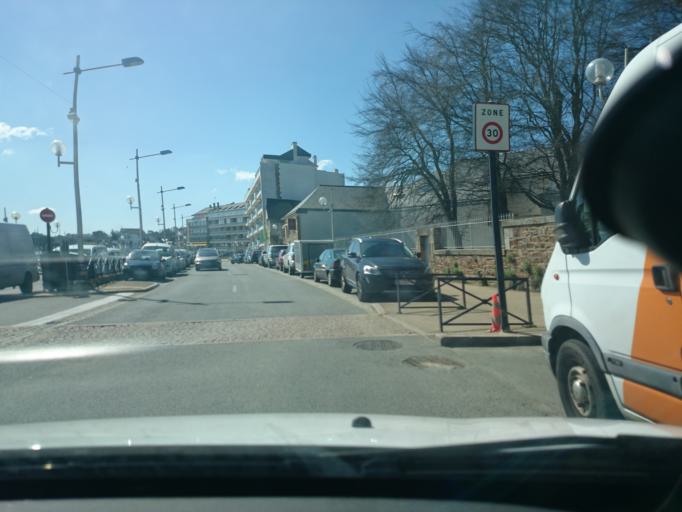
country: FR
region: Brittany
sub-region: Departement des Cotes-d'Armor
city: Perros-Guirec
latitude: 48.8050
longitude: -3.4428
